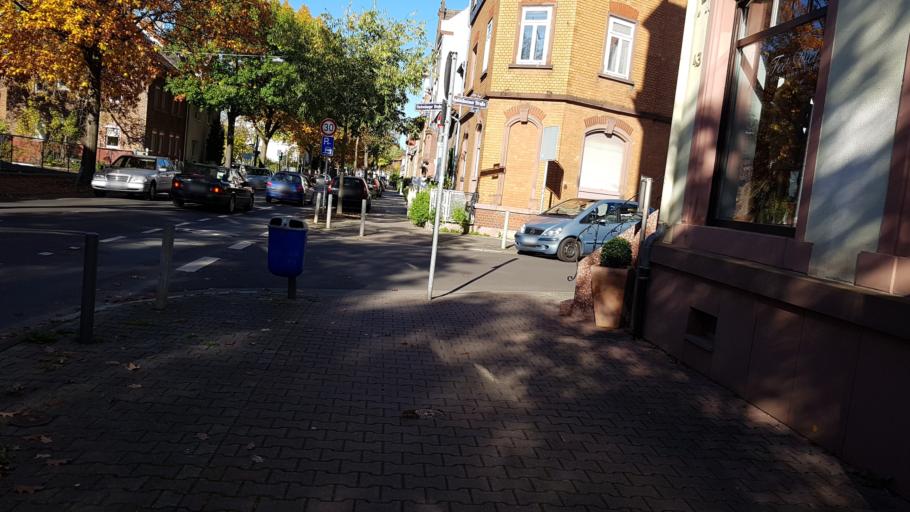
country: DE
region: Hesse
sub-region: Regierungsbezirk Darmstadt
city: Offenbach
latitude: 50.1184
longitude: 8.7712
